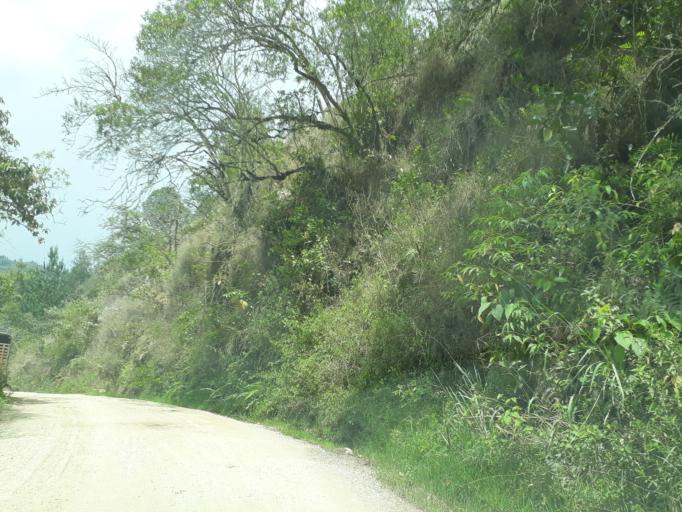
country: CO
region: Cundinamarca
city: Macheta
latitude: 5.0810
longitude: -73.5795
